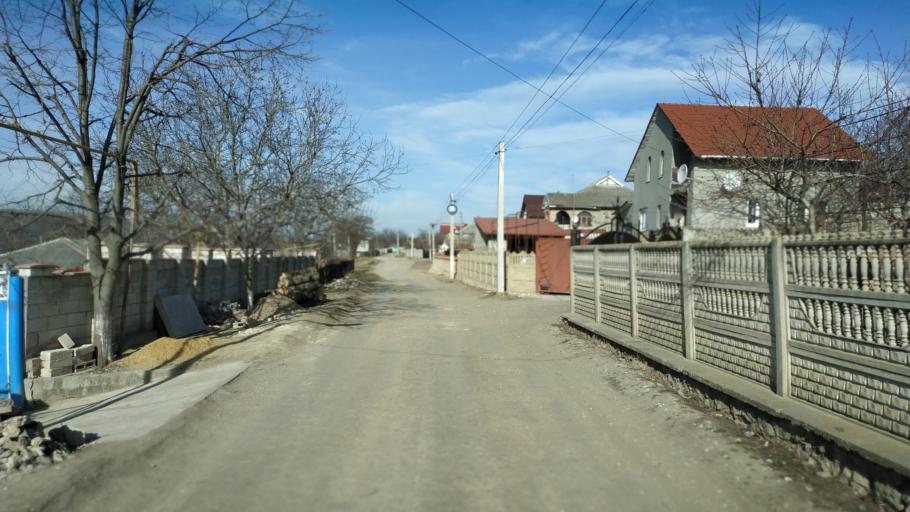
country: MD
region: Chisinau
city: Vatra
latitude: 47.0288
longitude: 28.6364
